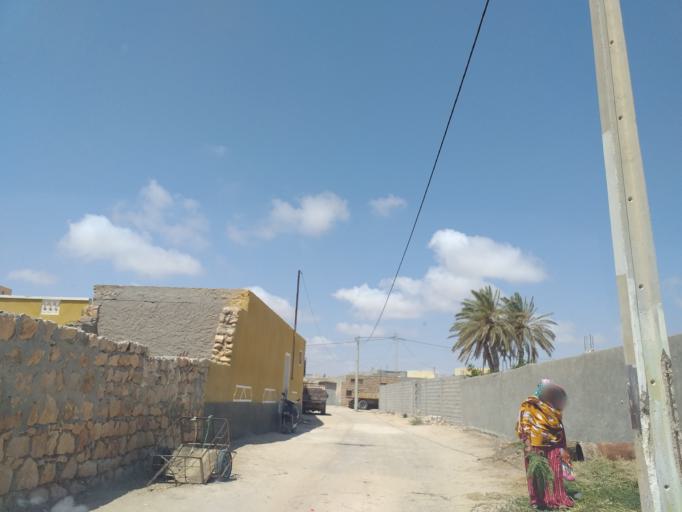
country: TN
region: Qabis
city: Gabes
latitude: 33.9479
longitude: 10.0583
